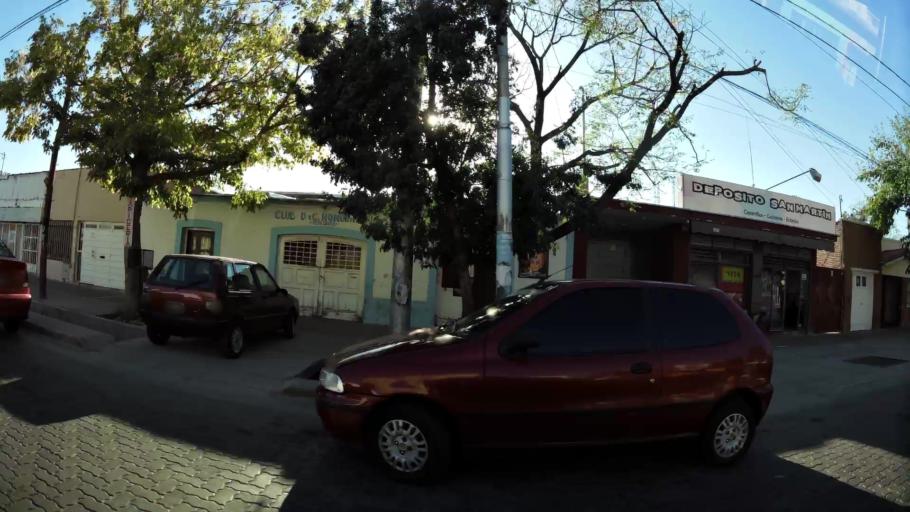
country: AR
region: Mendoza
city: Las Heras
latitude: -32.8600
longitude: -68.8330
